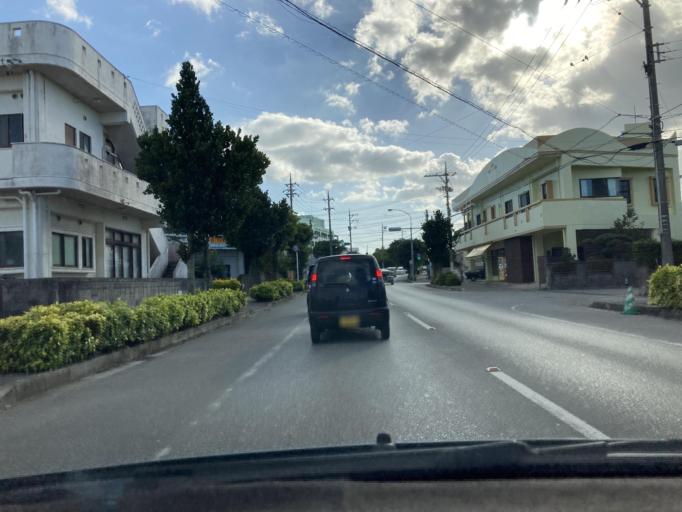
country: JP
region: Okinawa
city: Gushikawa
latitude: 26.3607
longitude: 127.8515
